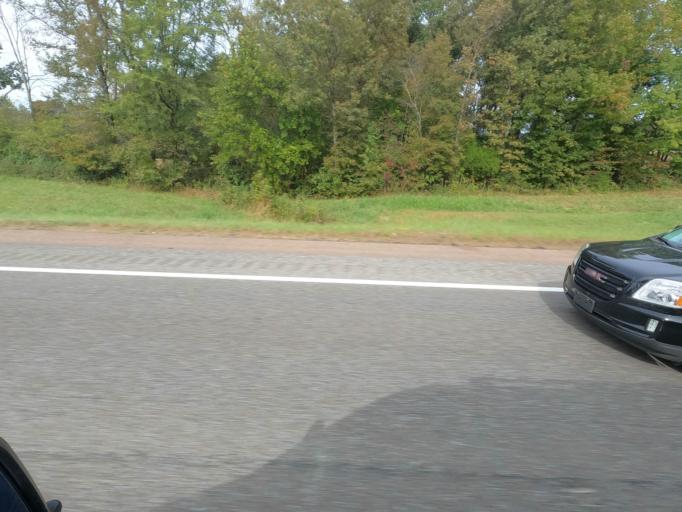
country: US
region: Tennessee
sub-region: Henderson County
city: Lexington
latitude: 35.7670
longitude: -88.4628
